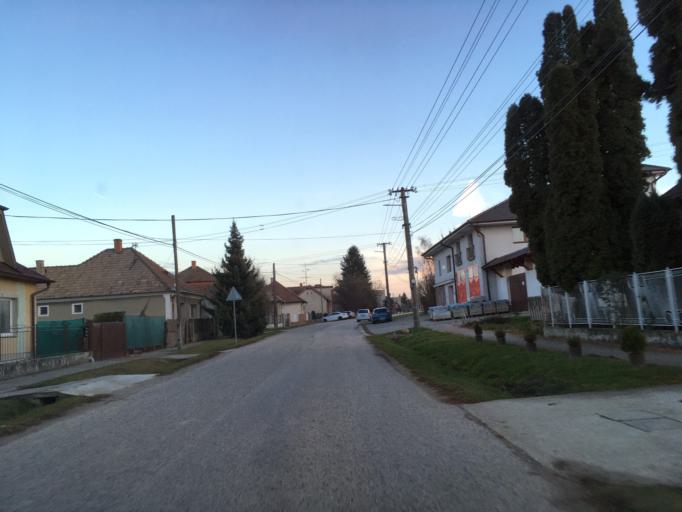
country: SK
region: Nitriansky
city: Svodin
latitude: 47.8720
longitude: 18.4596
